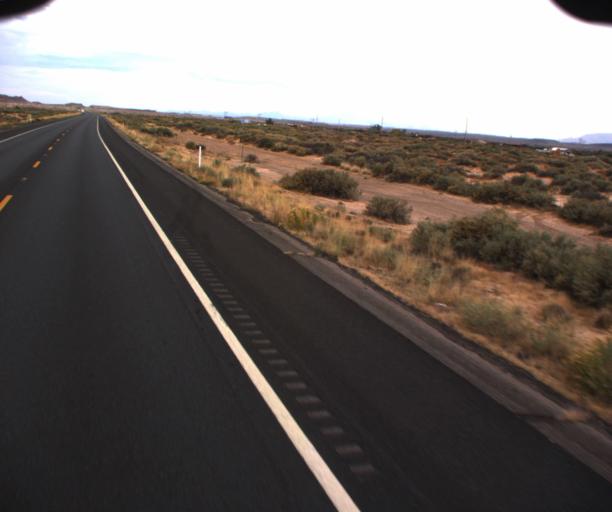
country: US
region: Arizona
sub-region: Coconino County
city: Tuba City
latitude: 36.0217
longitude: -111.3968
